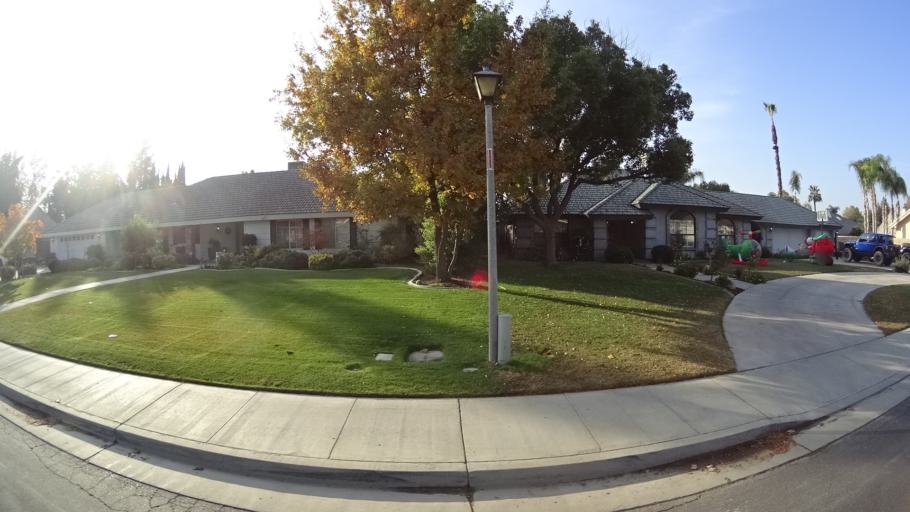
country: US
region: California
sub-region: Kern County
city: Rosedale
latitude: 35.3751
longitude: -119.1301
